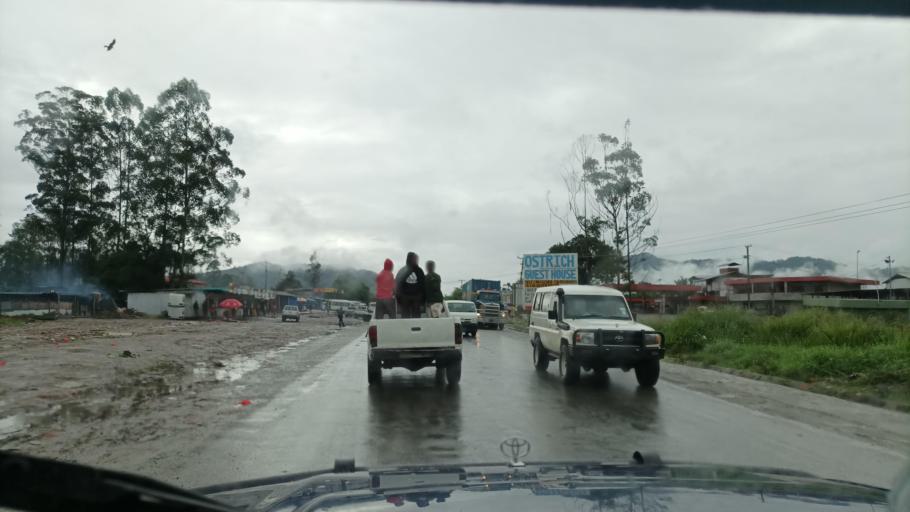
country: PG
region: Western Highlands
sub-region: Hagen
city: Mount Hagen
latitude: -5.8382
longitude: 144.3266
